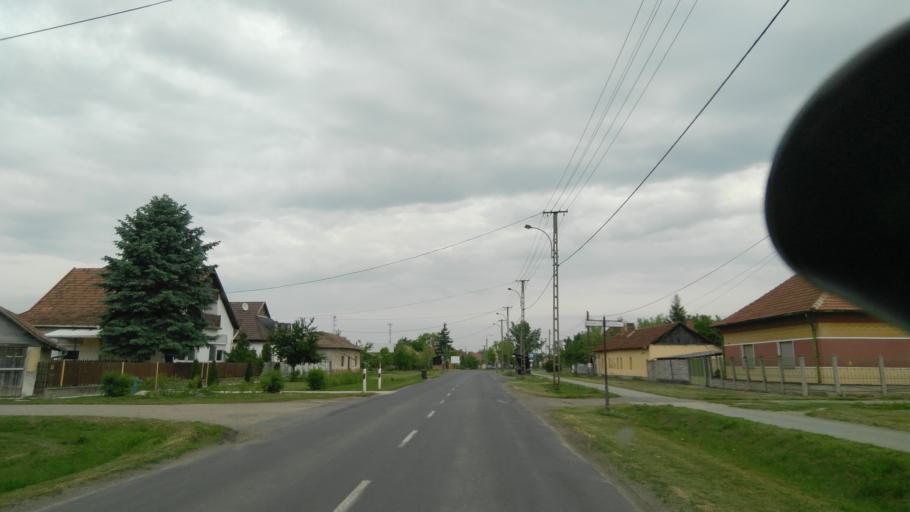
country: HU
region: Bekes
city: Veszto
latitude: 46.9109
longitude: 21.2581
